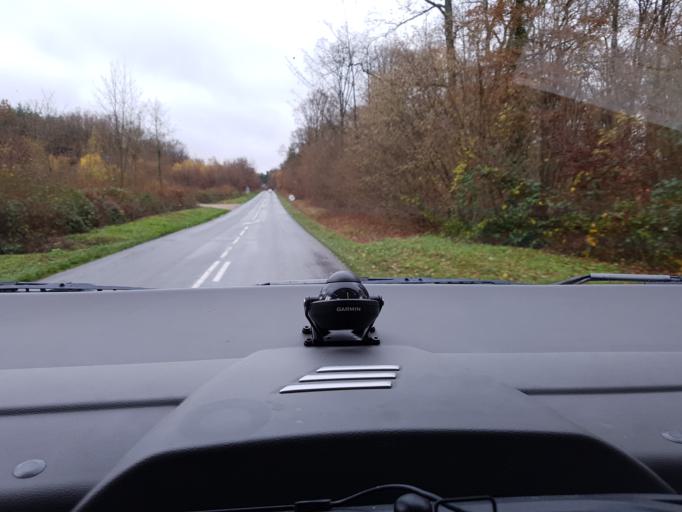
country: FR
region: Haute-Normandie
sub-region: Departement de l'Eure
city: Pont-Saint-Pierre
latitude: 49.3252
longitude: 1.2917
